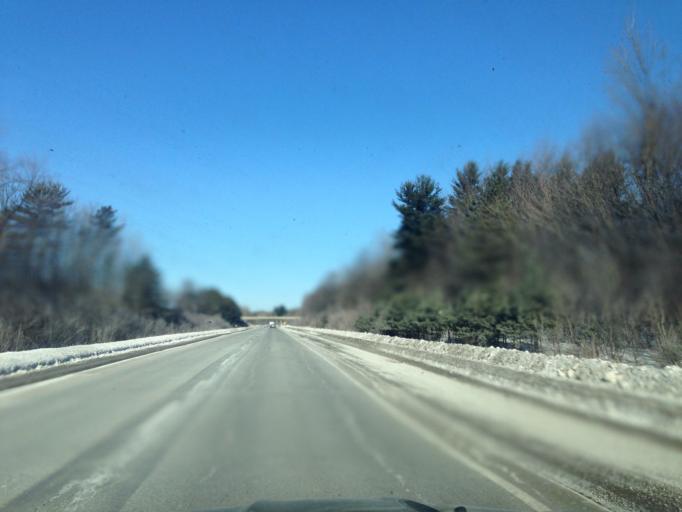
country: CA
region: Ontario
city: Ottawa
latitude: 45.3579
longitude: -75.4720
